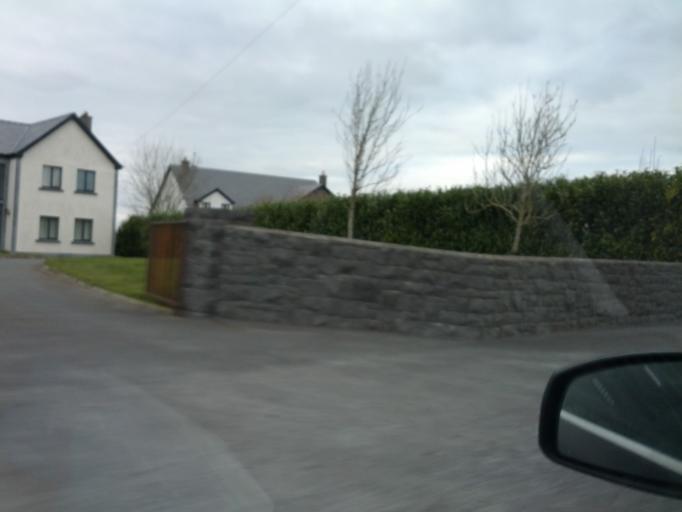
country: IE
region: Connaught
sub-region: County Galway
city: Oranmore
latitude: 53.2529
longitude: -8.8407
